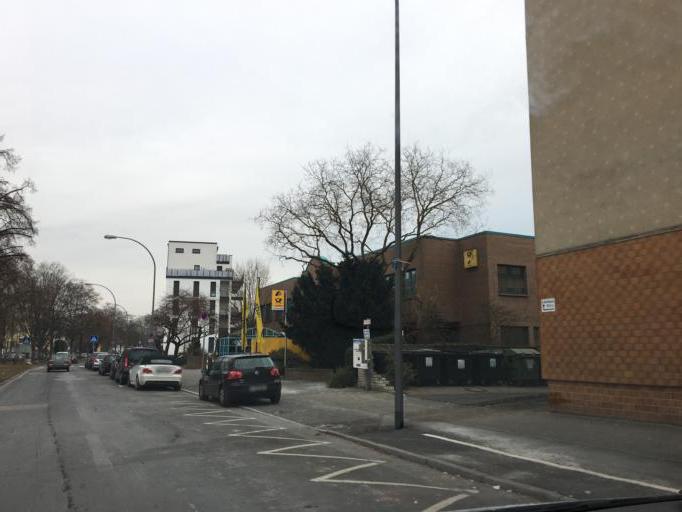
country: DE
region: Hesse
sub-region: Regierungsbezirk Darmstadt
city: Frankfurt am Main
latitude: 50.1466
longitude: 8.6597
